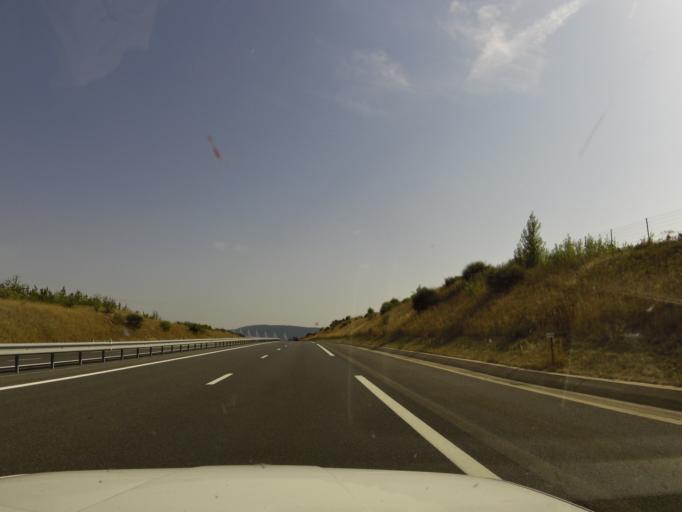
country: FR
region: Midi-Pyrenees
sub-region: Departement de l'Aveyron
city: Creissels
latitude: 44.1231
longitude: 3.0302
